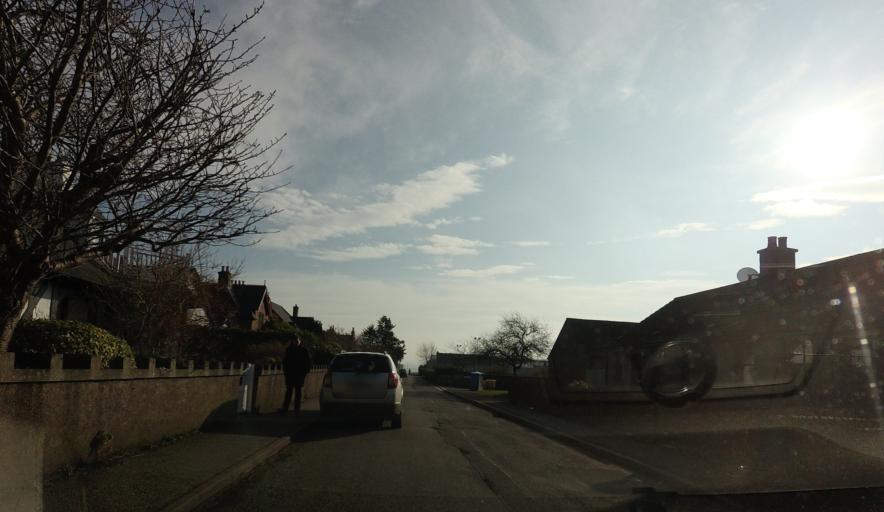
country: GB
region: Scotland
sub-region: Highland
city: Fortrose
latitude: 57.5816
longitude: -4.1283
